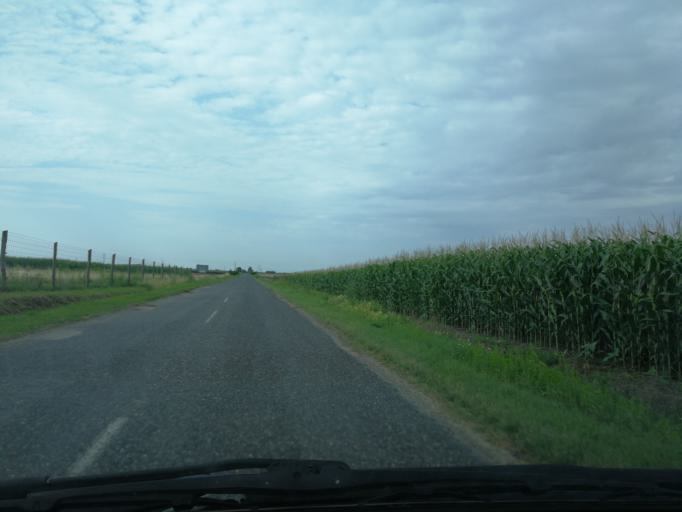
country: HU
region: Bacs-Kiskun
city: Kalocsa
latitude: 46.4912
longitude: 19.0519
